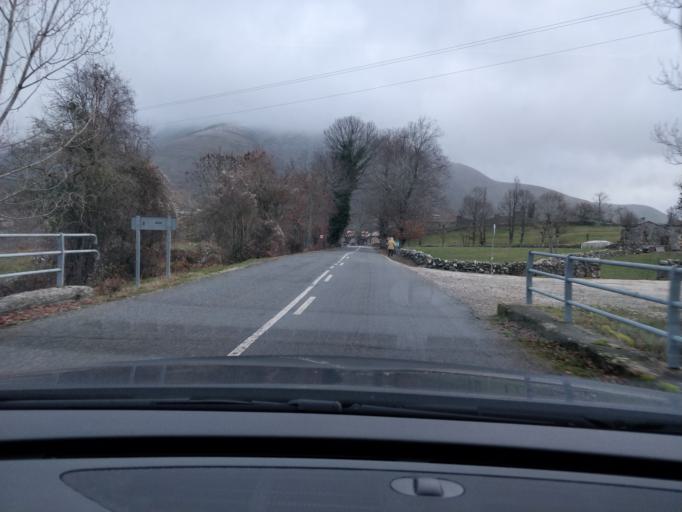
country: ES
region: Castille and Leon
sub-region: Provincia de Burgos
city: Espinosa de los Monteros
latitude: 43.1182
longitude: -3.5943
